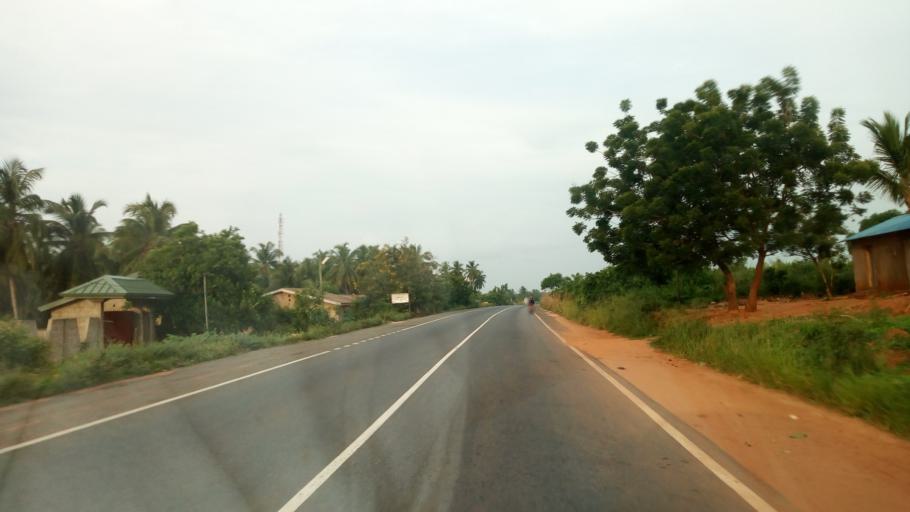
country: TG
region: Maritime
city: Lome
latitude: 6.0981
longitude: 1.0921
